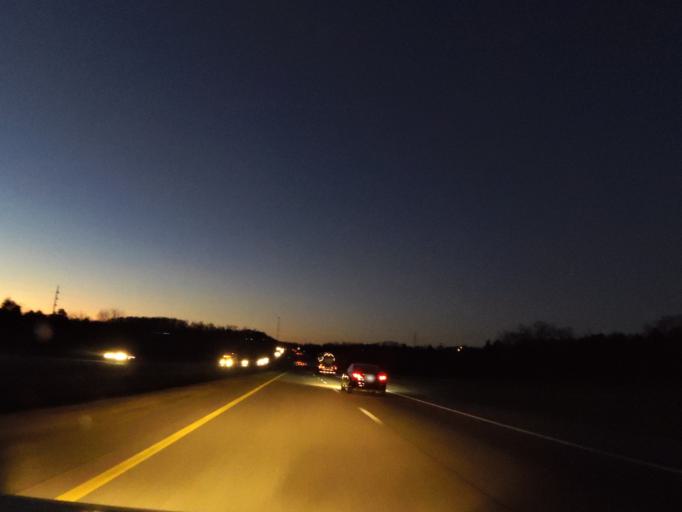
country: US
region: Tennessee
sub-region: Jefferson County
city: Dandridge
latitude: 36.0460
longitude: -83.3433
